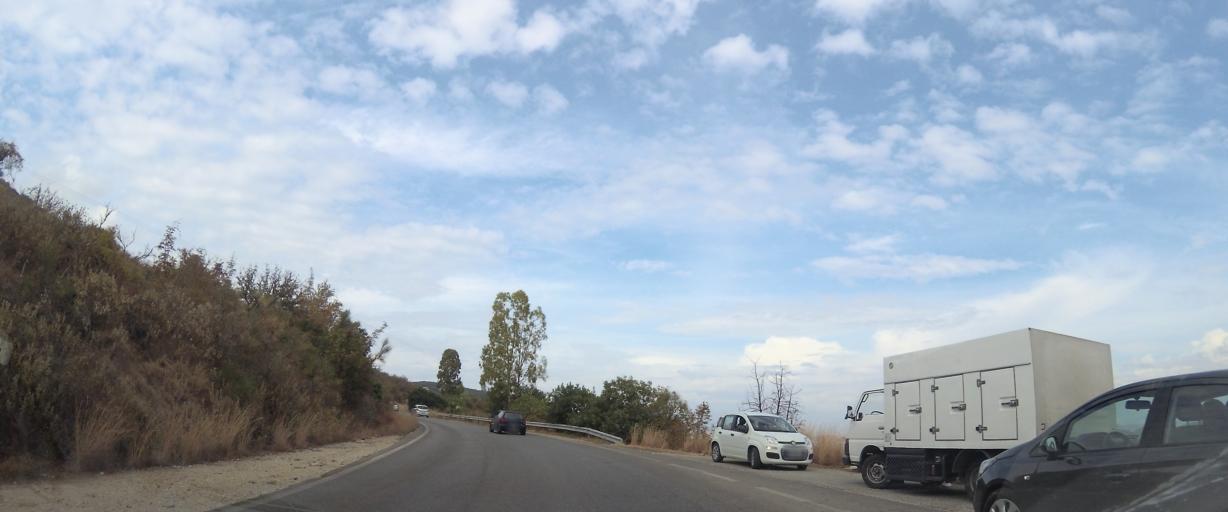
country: AL
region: Vlore
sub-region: Rrethi i Sarandes
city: Xarre
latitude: 39.7480
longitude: 19.9384
